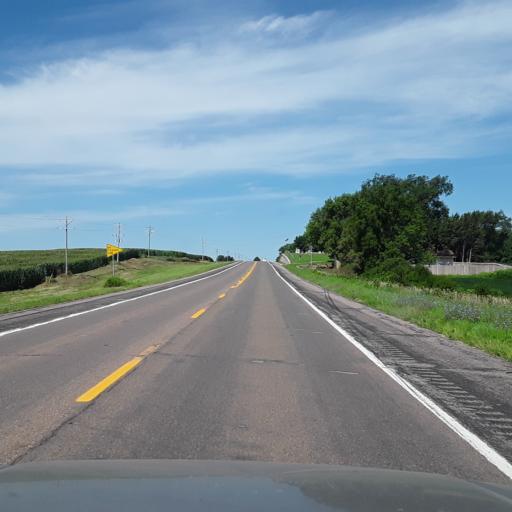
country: US
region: Nebraska
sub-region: Seward County
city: Seward
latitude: 40.9016
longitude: -97.1414
